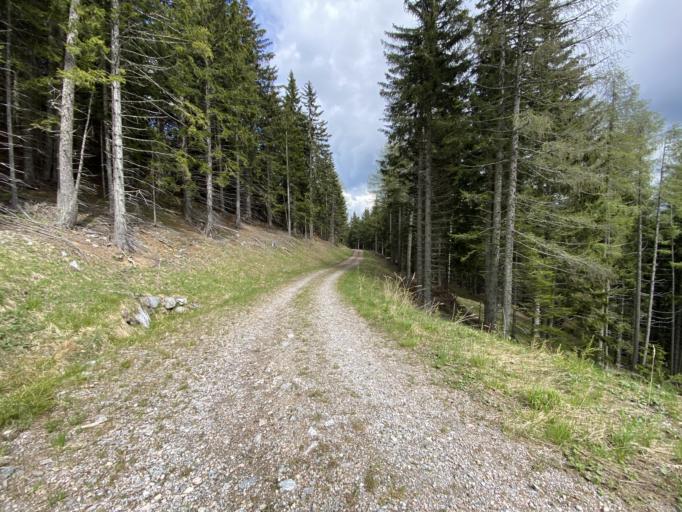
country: AT
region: Styria
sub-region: Politischer Bezirk Bruck-Muerzzuschlag
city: Spital am Semmering
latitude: 47.6809
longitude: 15.7122
